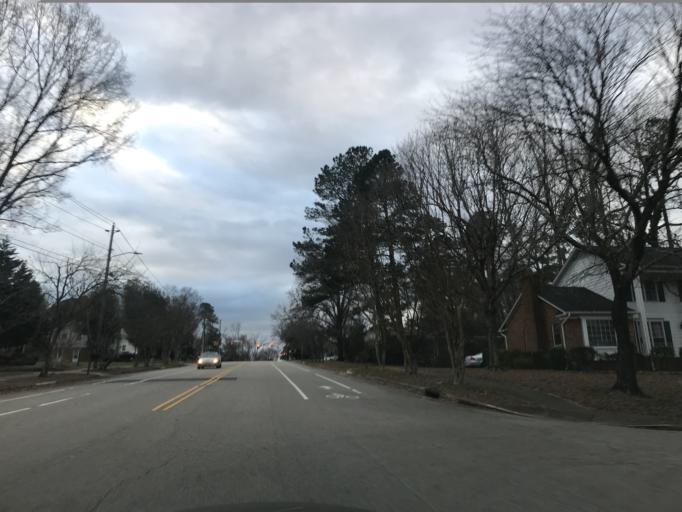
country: US
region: North Carolina
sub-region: Wake County
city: West Raleigh
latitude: 35.8544
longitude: -78.6578
